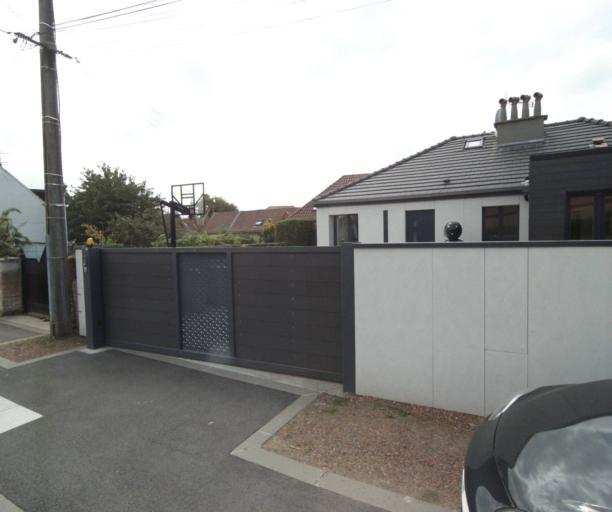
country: FR
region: Nord-Pas-de-Calais
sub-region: Departement du Nord
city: Chereng
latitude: 50.6176
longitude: 3.2113
